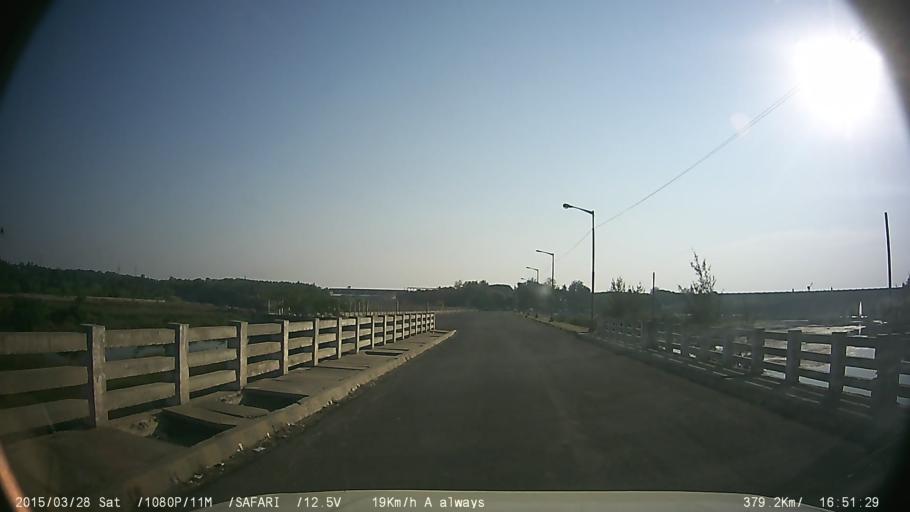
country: IN
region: Karnataka
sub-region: Mandya
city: Shrirangapattana
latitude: 12.4257
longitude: 76.5798
